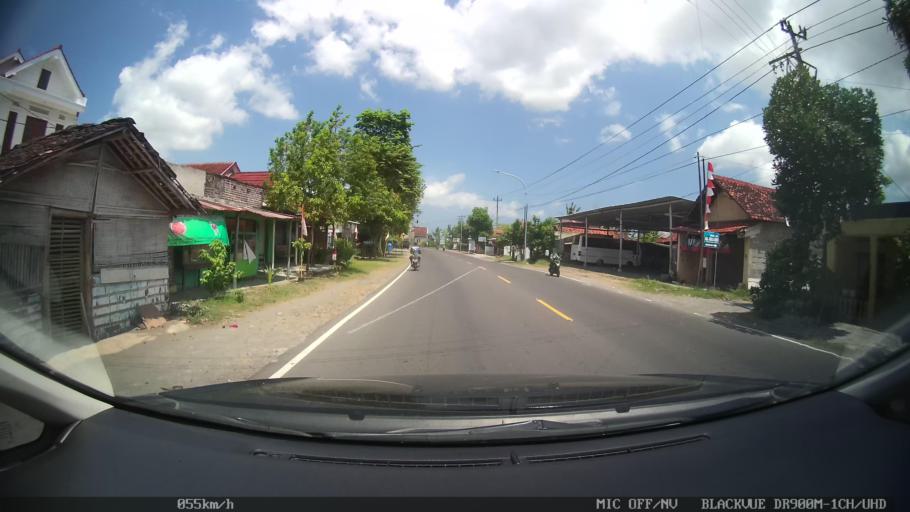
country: ID
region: Daerah Istimewa Yogyakarta
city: Sewon
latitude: -7.8860
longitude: 110.3466
